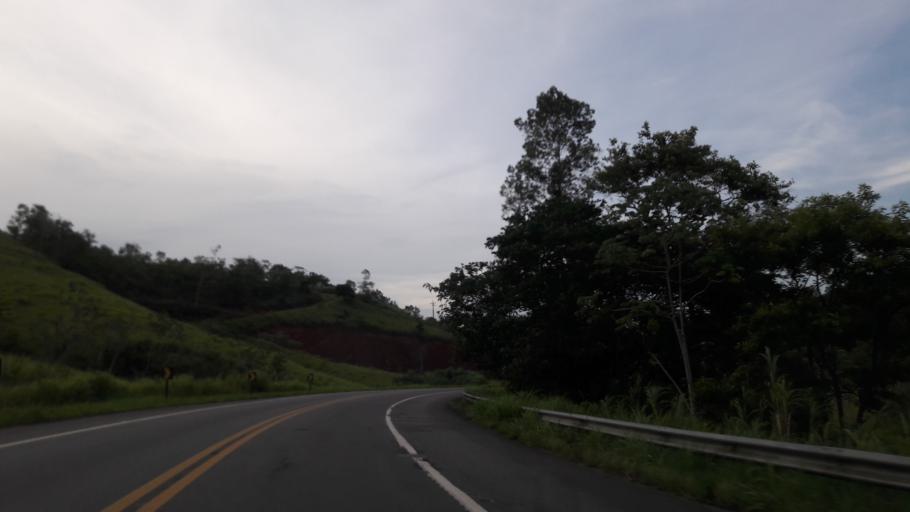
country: BR
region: Sao Paulo
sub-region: Miracatu
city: Miracatu
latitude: -24.2751
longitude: -47.2612
